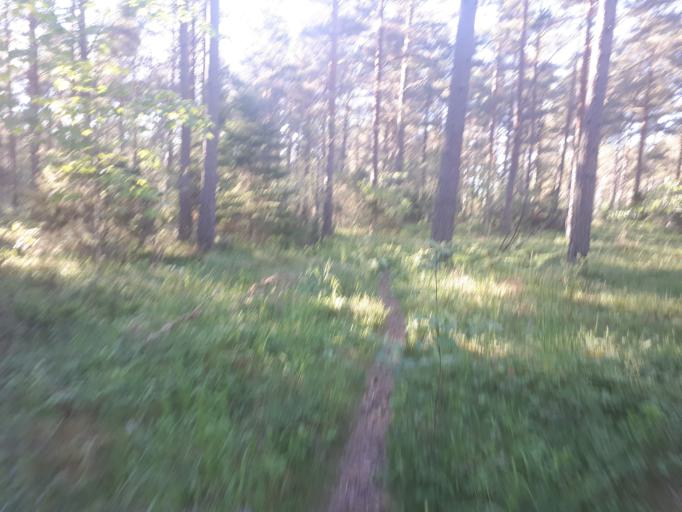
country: SE
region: Gotland
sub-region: Gotland
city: Visby
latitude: 57.6035
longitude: 18.2902
